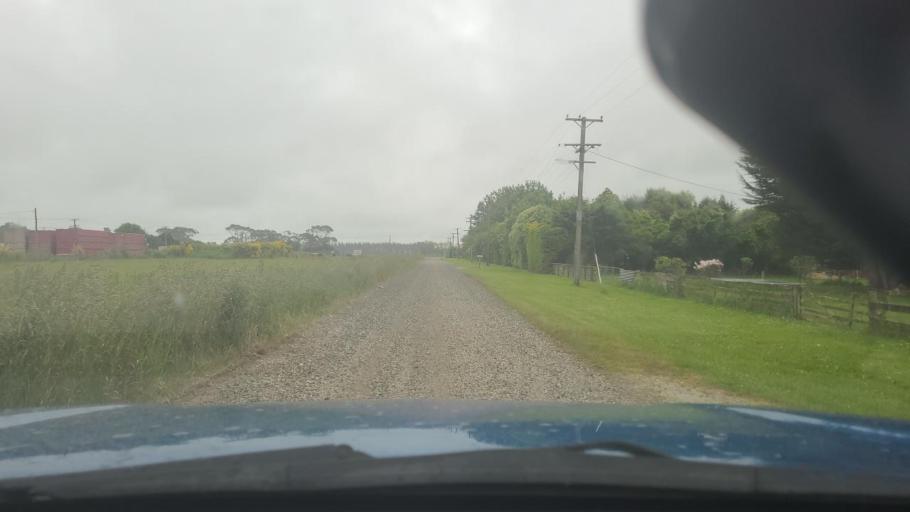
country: NZ
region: Southland
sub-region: Invercargill City
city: Invercargill
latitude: -46.3407
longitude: 168.6555
